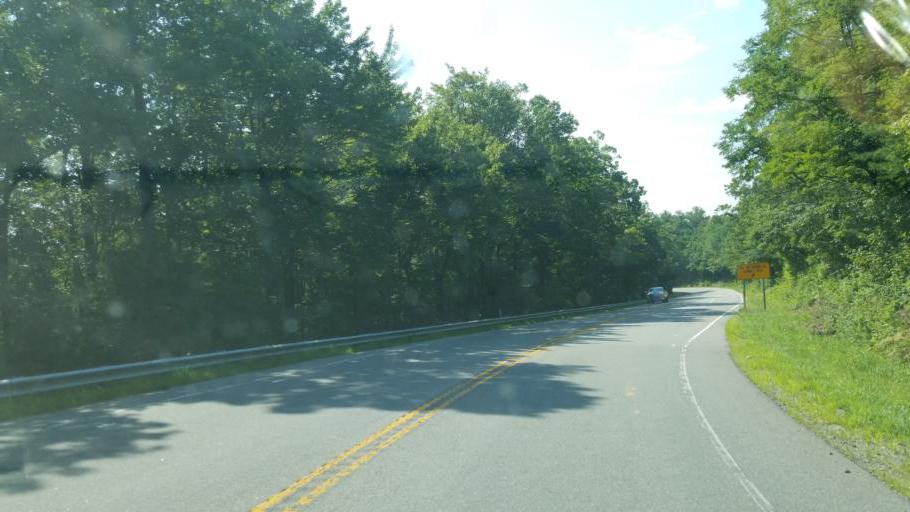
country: US
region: North Carolina
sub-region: Avery County
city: Newland
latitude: 35.9348
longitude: -81.8273
